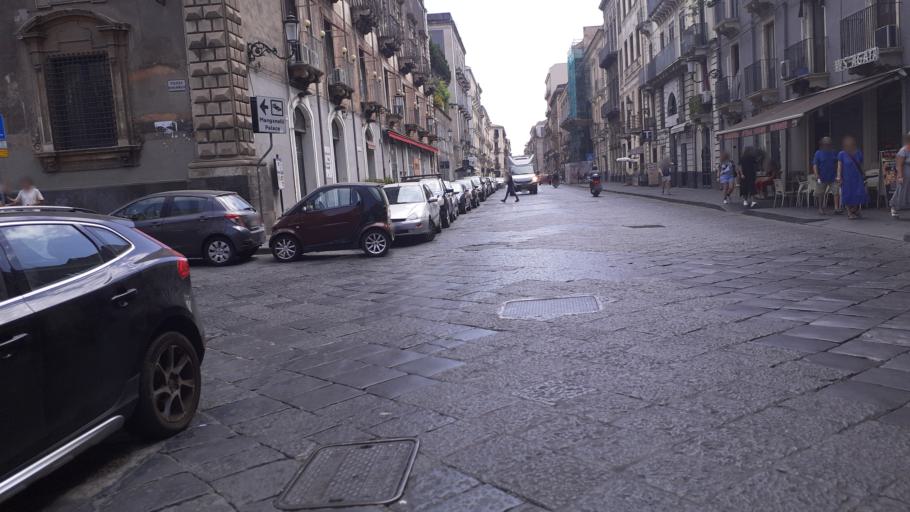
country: IT
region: Sicily
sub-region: Catania
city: Catania
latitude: 37.5049
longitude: 15.0877
